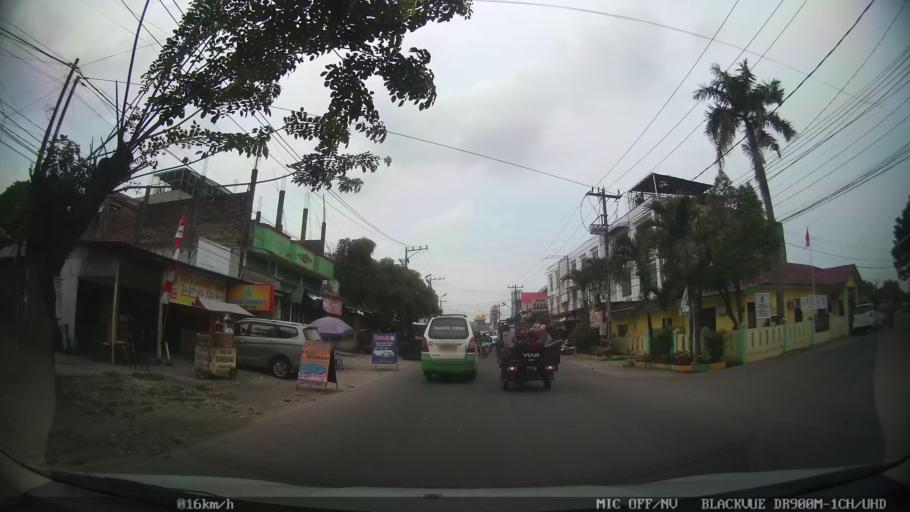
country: ID
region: North Sumatra
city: Medan
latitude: 3.5801
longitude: 98.7293
